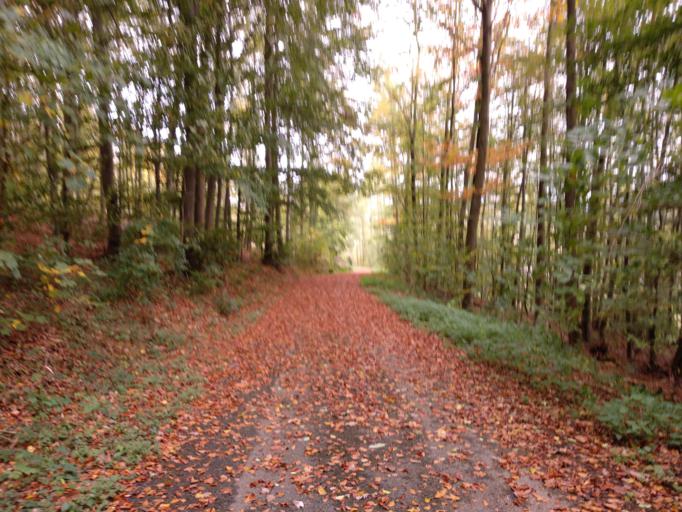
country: DE
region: North Rhine-Westphalia
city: Beverungen
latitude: 51.6625
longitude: 9.3498
